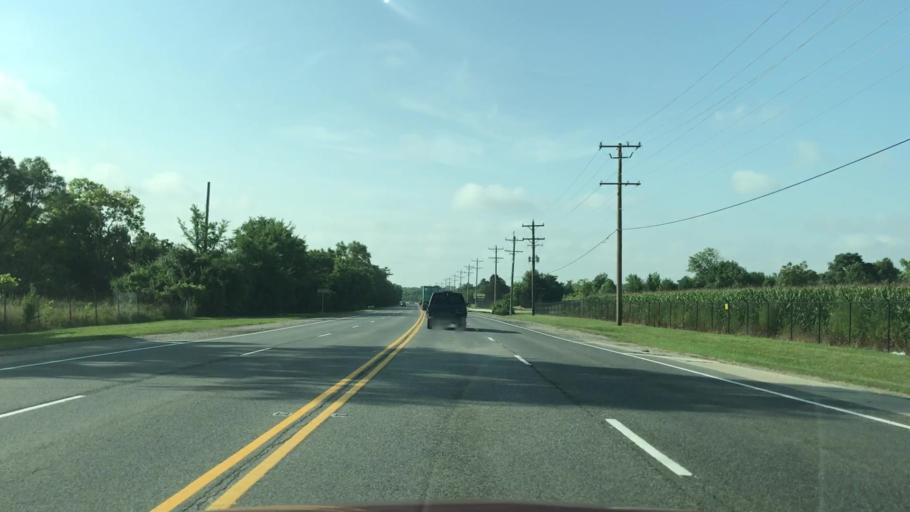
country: US
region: Illinois
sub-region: Will County
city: Romeoville
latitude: 41.6232
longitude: -88.0798
